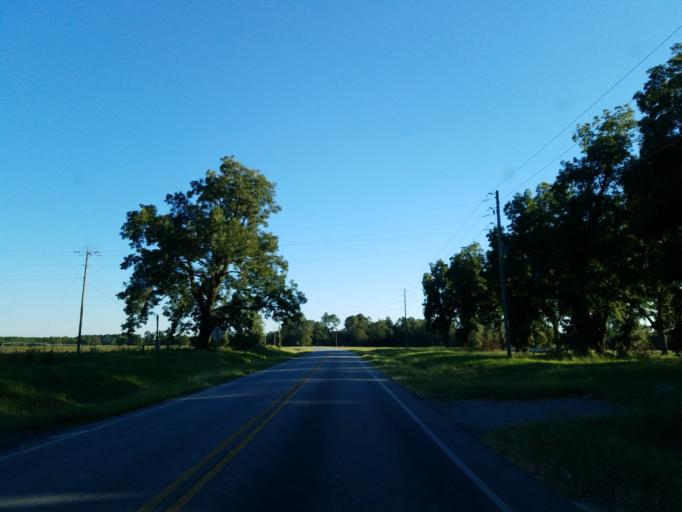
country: US
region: Georgia
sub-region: Worth County
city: Sylvester
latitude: 31.6784
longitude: -83.8778
